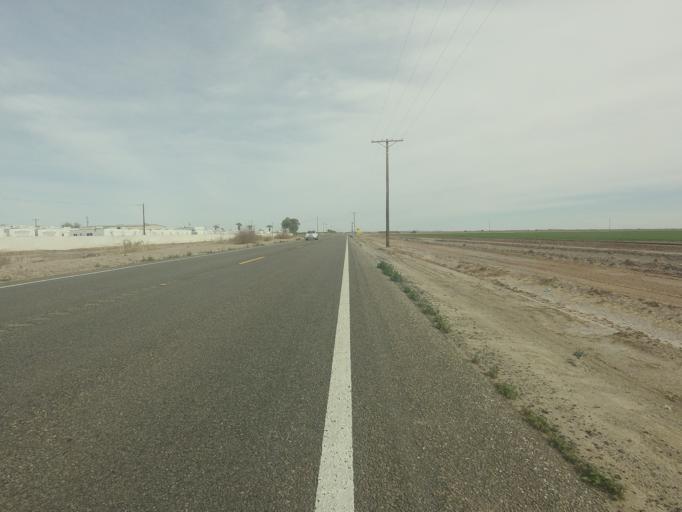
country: US
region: California
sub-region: Imperial County
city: Holtville
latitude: 32.9747
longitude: -115.3273
